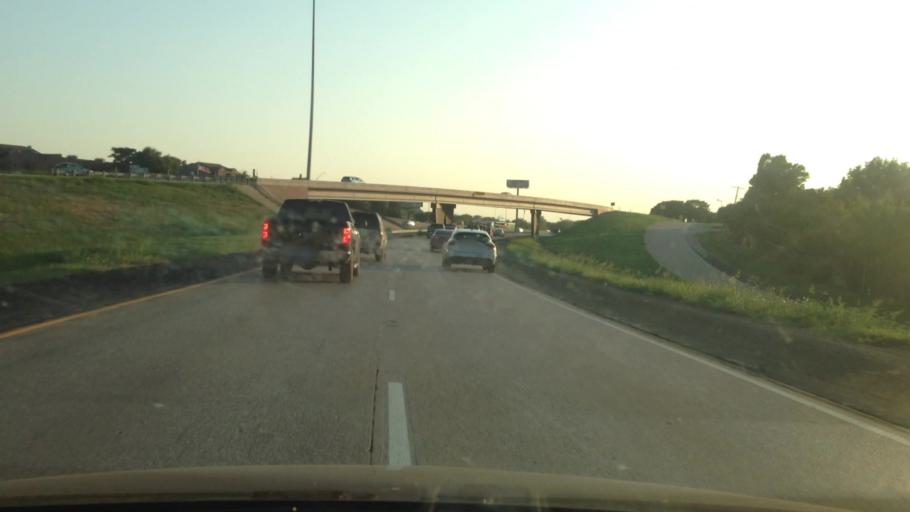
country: US
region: Texas
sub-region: Tarrant County
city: Kennedale
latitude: 32.6701
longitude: -97.2150
